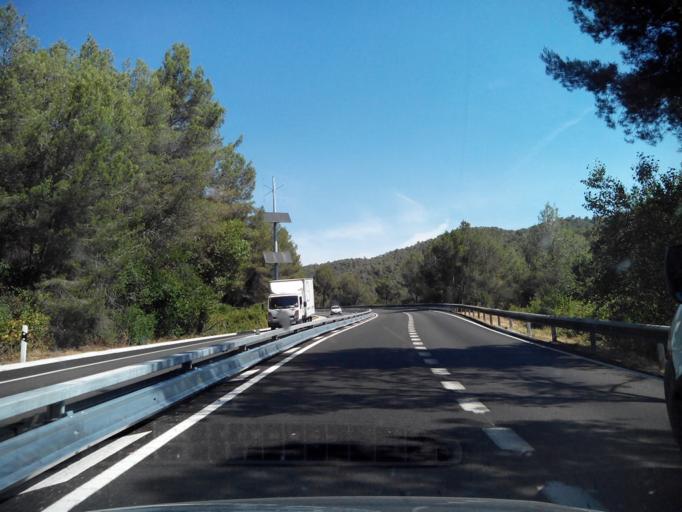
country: ES
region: Catalonia
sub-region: Provincia de Barcelona
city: Viladecavalls
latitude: 41.5768
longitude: 1.9605
